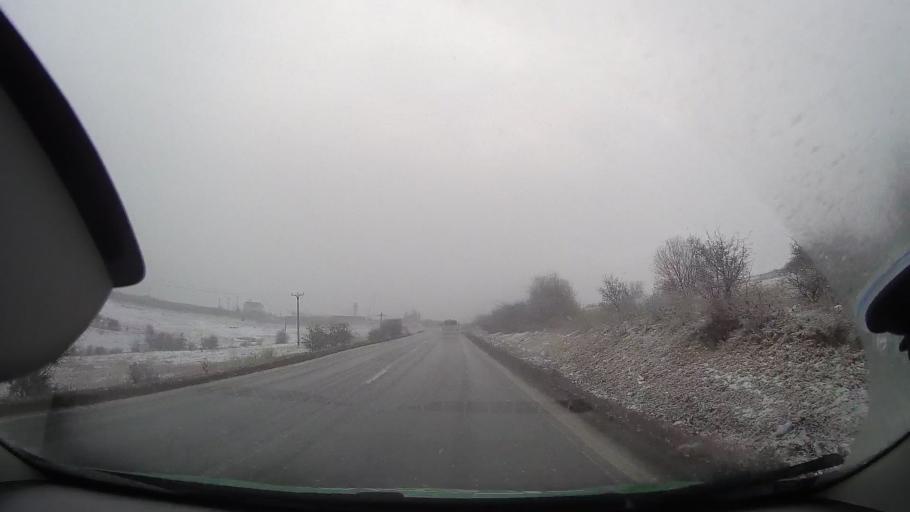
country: RO
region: Mures
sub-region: Comuna Bagaciu
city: Delenii
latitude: 46.2586
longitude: 24.3000
